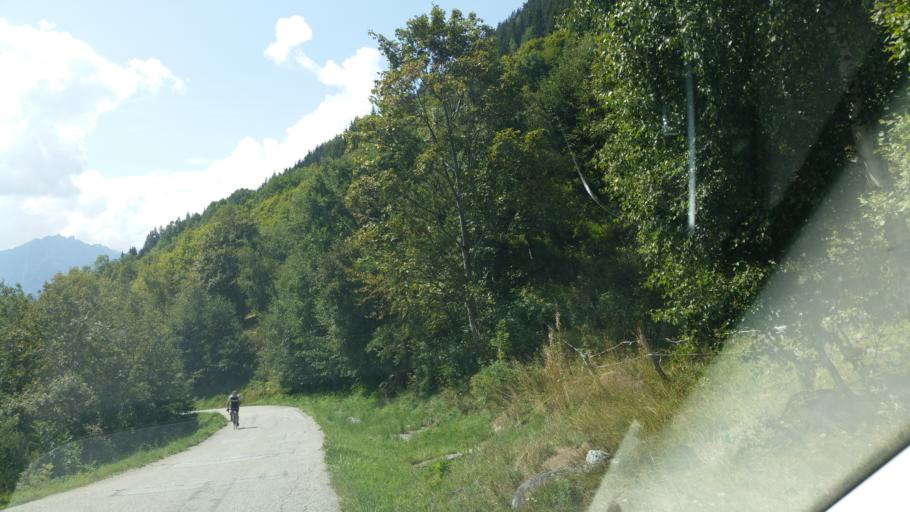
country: FR
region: Rhone-Alpes
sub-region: Departement de la Savoie
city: La Chambre
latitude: 45.4106
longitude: 6.3367
